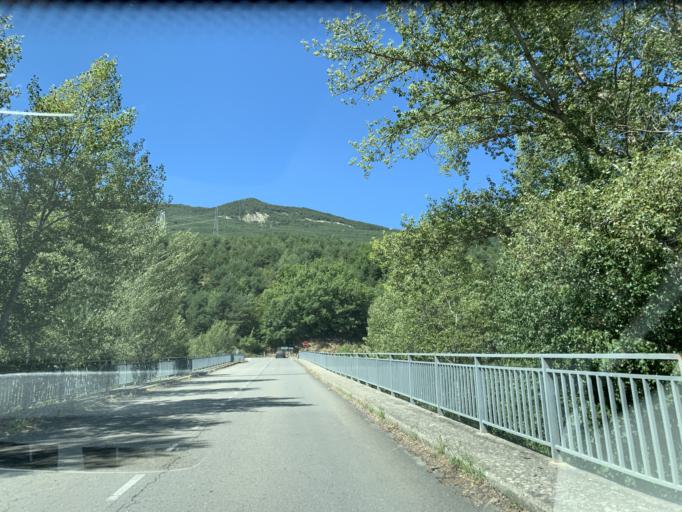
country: ES
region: Aragon
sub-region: Provincia de Huesca
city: Biescas
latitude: 42.5788
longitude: -0.3236
